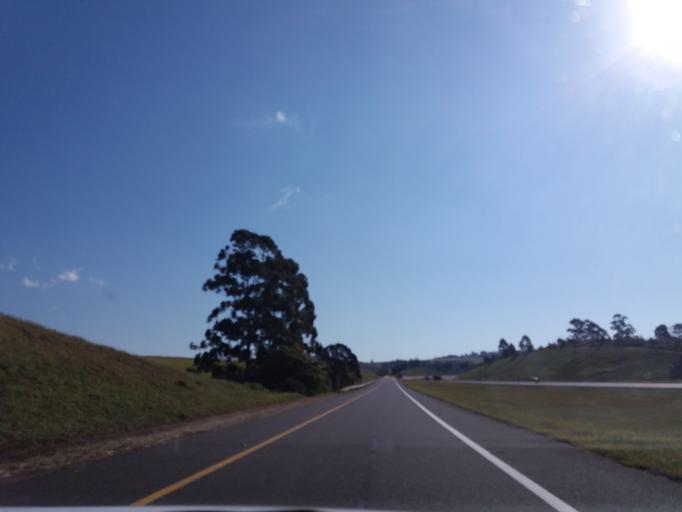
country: ZA
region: KwaZulu-Natal
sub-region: eThekwini Metropolitan Municipality
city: Mpumalanga
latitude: -29.8046
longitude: 30.7449
